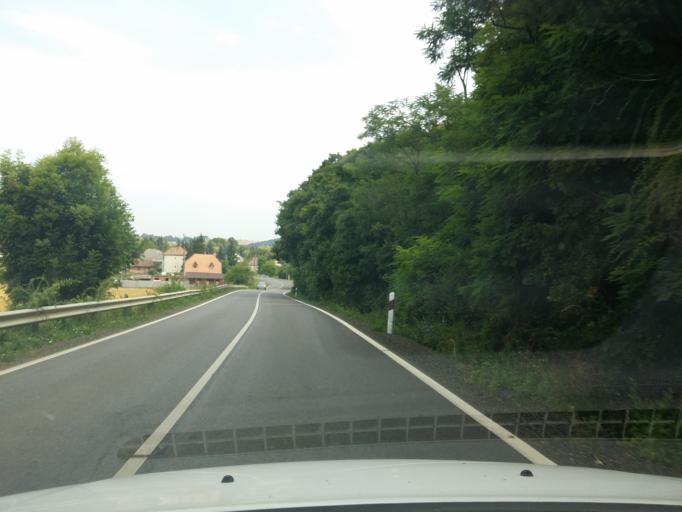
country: HU
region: Pest
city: Acsa
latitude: 47.7697
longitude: 19.3707
